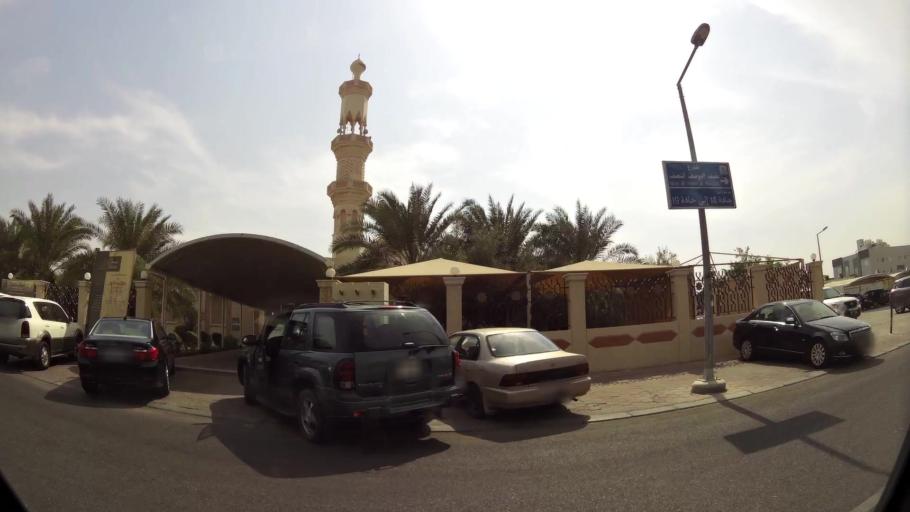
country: KW
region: Al Asimah
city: Kuwait City
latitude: 29.3571
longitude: 47.9814
